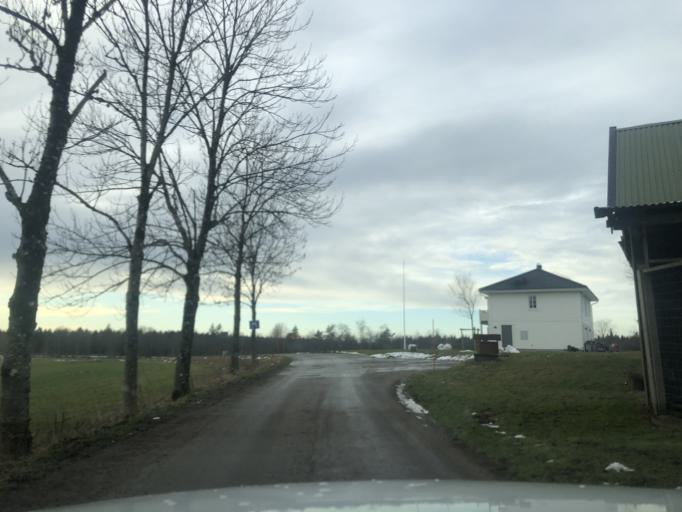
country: SE
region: Vaestra Goetaland
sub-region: Ulricehamns Kommun
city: Ulricehamn
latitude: 57.8050
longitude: 13.5083
